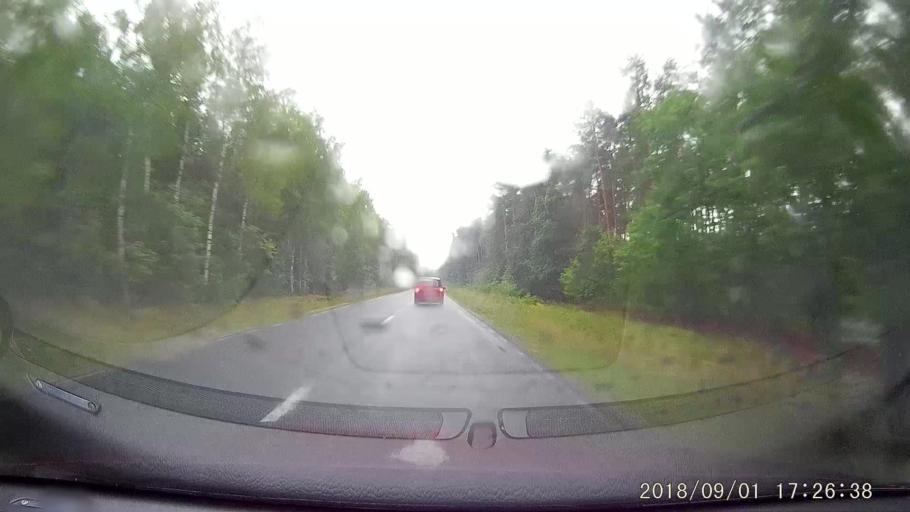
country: PL
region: Lubusz
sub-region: Powiat zaganski
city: Zagan
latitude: 51.6754
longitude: 15.3085
